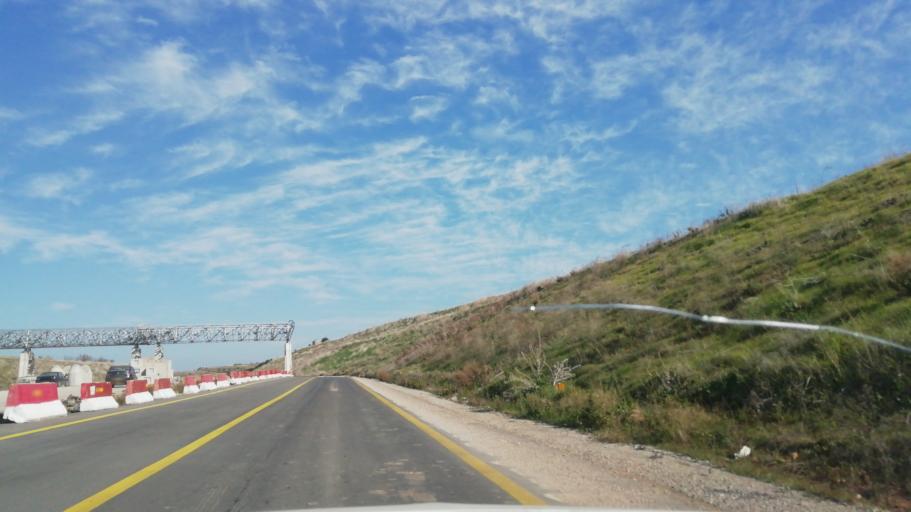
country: DZ
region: Tlemcen
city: Bensekrane
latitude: 34.9829
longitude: -1.2191
